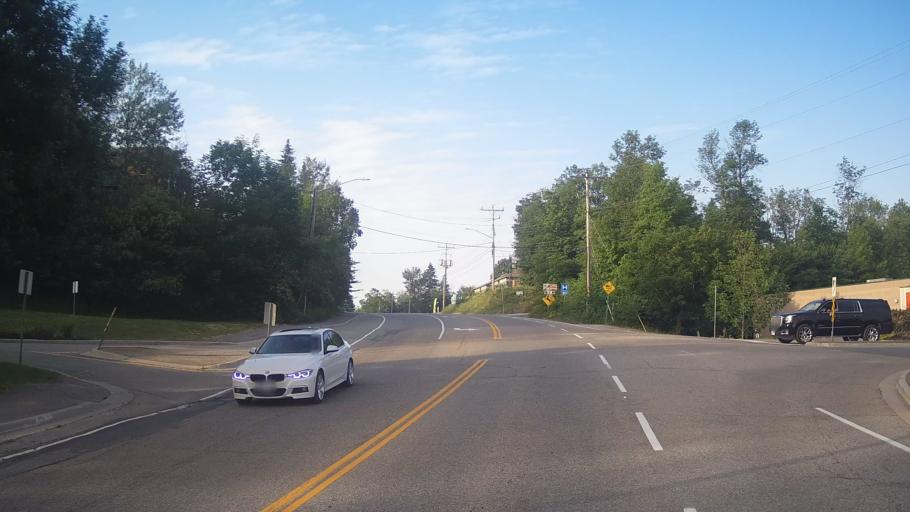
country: CA
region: Ontario
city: Huntsville
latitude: 45.3376
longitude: -79.2033
